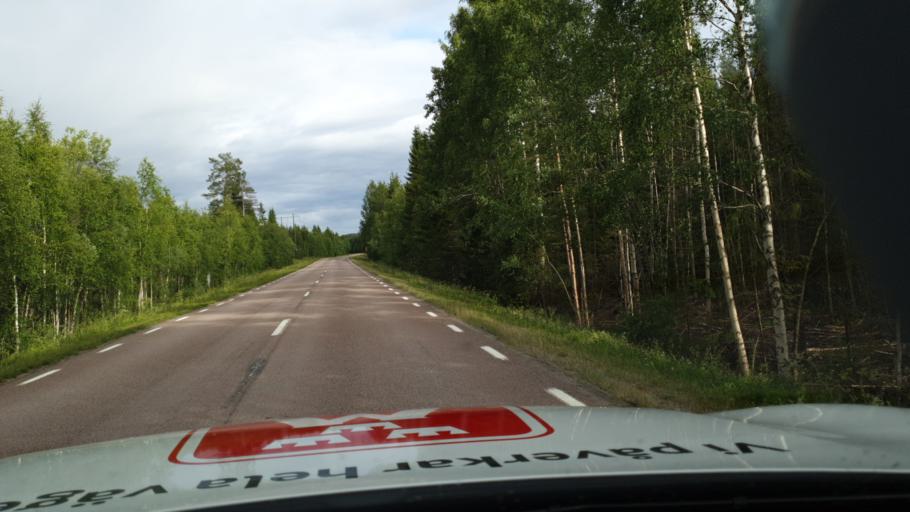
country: SE
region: Jaemtland
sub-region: Stroemsunds Kommun
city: Stroemsund
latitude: 63.6403
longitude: 16.0238
